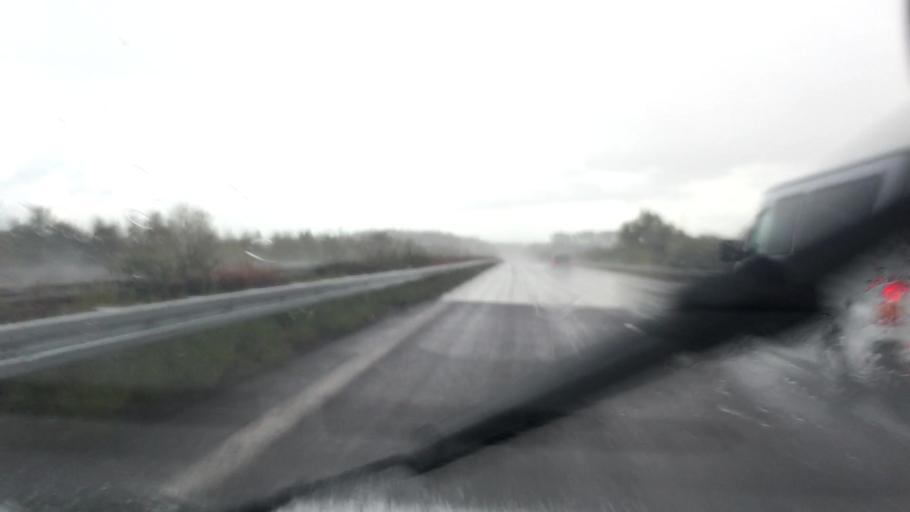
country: DE
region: Saxony-Anhalt
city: Eickendorf
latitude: 51.9580
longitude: 11.6800
